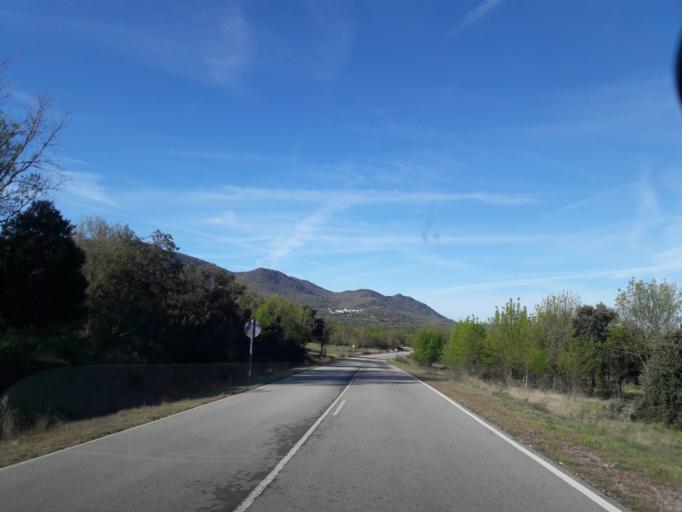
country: ES
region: Castille and Leon
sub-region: Provincia de Salamanca
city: Ledrada
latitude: 40.4601
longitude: -5.7276
